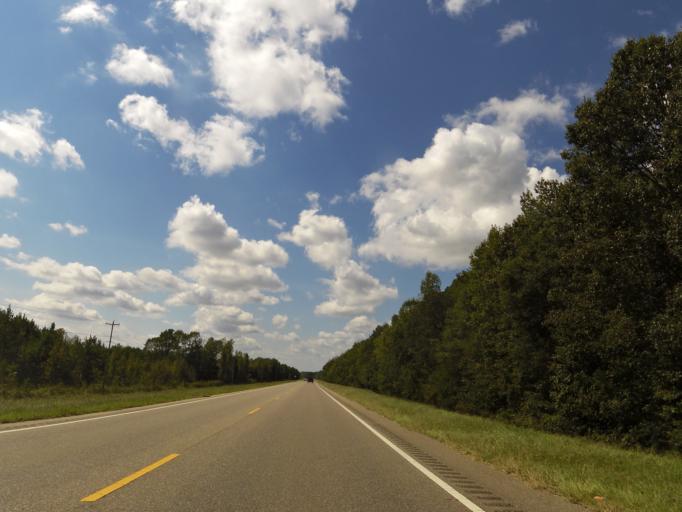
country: US
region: Alabama
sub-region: Dallas County
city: Selma
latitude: 32.3656
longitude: -87.1165
